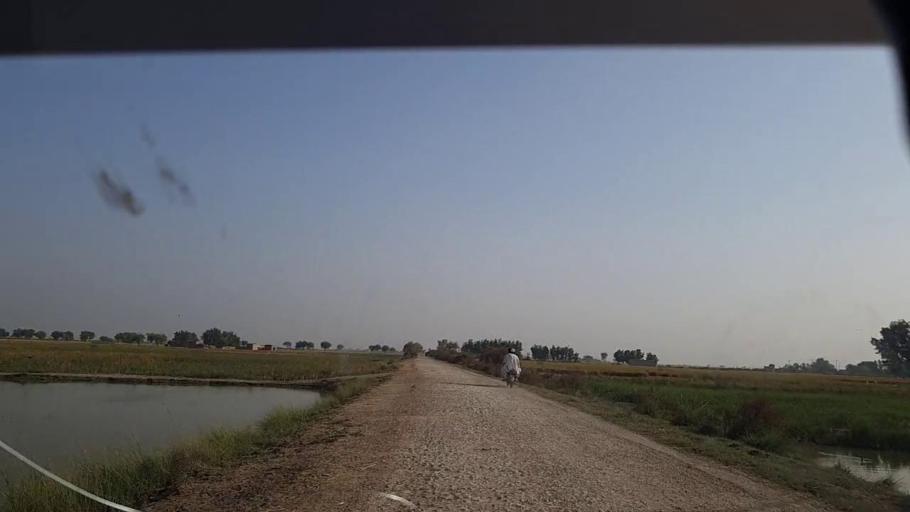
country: PK
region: Sindh
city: Shikarpur
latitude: 28.0655
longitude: 68.5470
